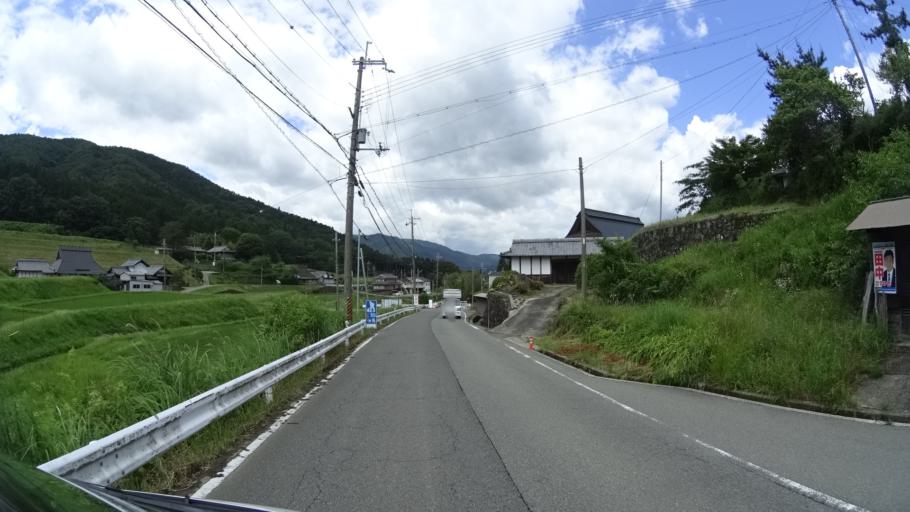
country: JP
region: Kyoto
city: Kameoka
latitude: 35.0115
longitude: 135.4494
